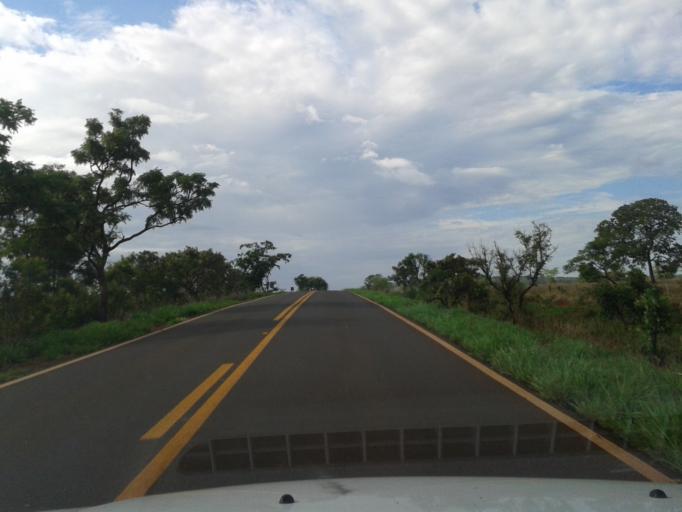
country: BR
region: Minas Gerais
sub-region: Ituiutaba
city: Ituiutaba
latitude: -19.1449
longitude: -49.7766
